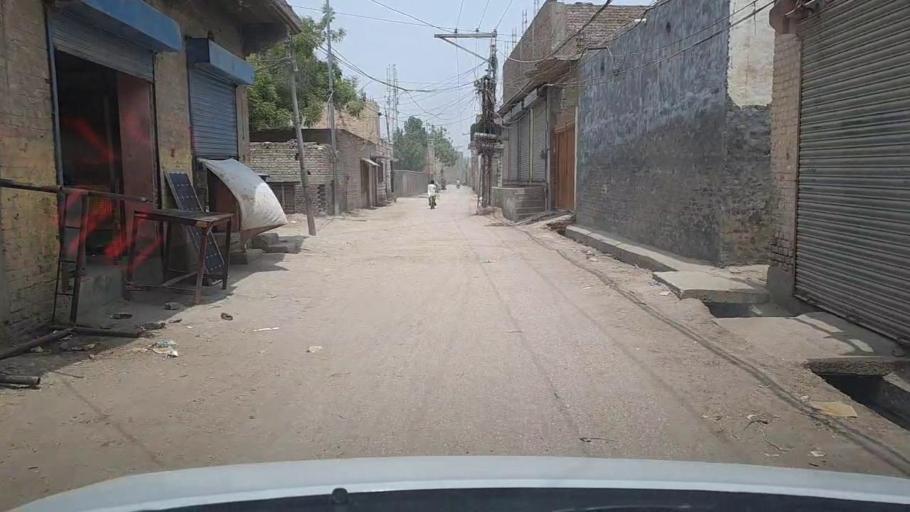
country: PK
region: Sindh
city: Sita Road
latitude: 27.0386
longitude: 67.8458
